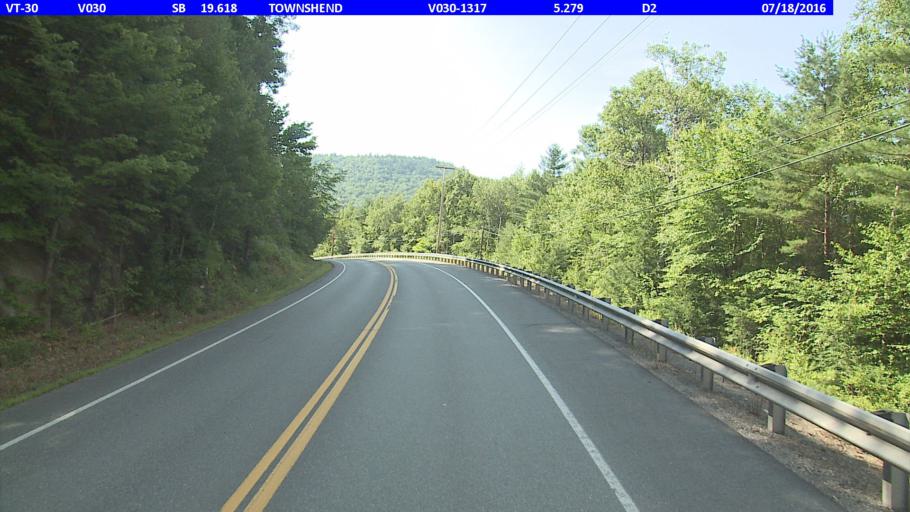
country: US
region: Vermont
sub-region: Windham County
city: Newfane
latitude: 43.0686
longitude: -72.7035
